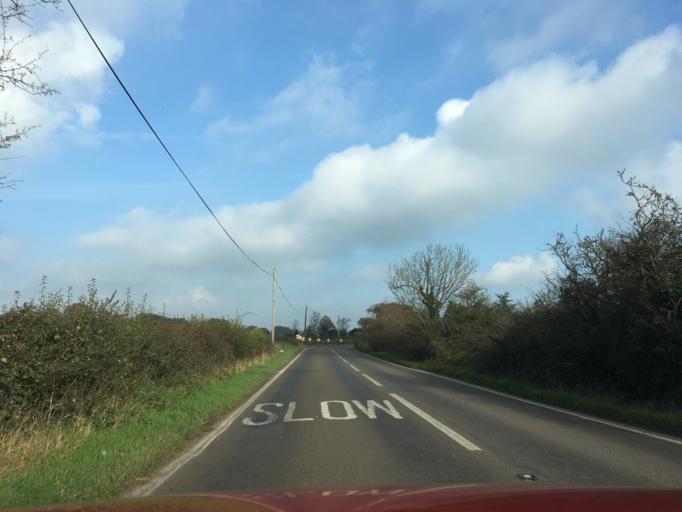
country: GB
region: England
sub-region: South Gloucestershire
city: Tytherington
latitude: 51.5917
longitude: -2.4478
